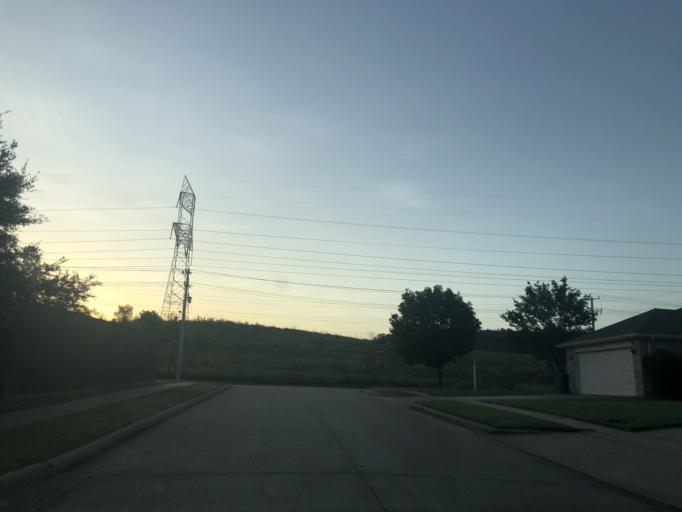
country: US
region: Texas
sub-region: Dallas County
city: Duncanville
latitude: 32.6567
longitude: -96.9619
